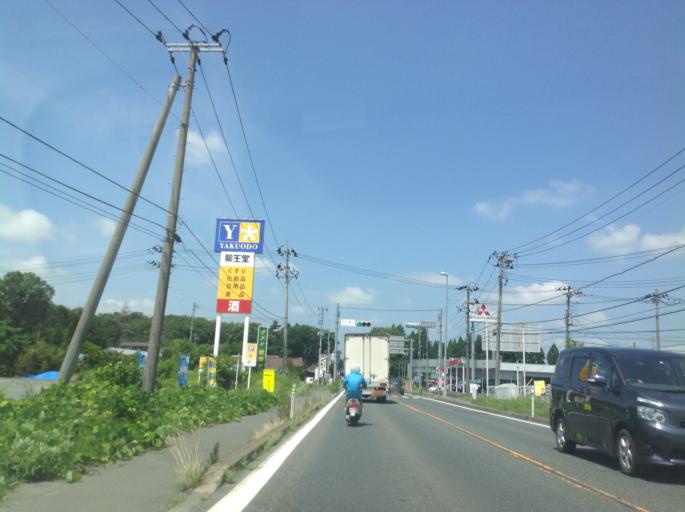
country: JP
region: Iwate
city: Hanamaki
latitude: 39.3385
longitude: 141.1083
